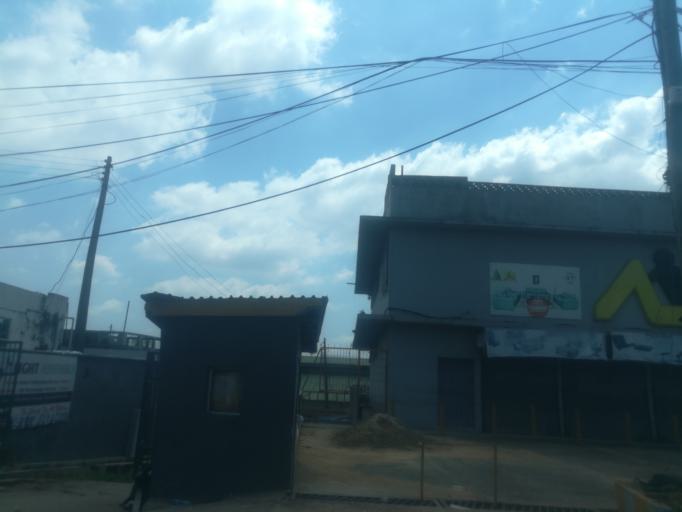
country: NG
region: Oyo
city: Ibadan
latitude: 7.3876
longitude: 3.8763
